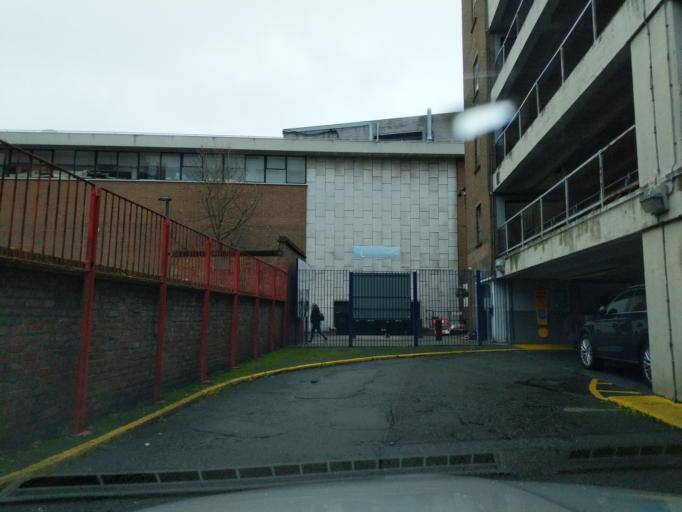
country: GB
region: England
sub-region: Hertfordshire
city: Watford
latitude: 51.6578
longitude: -0.4005
